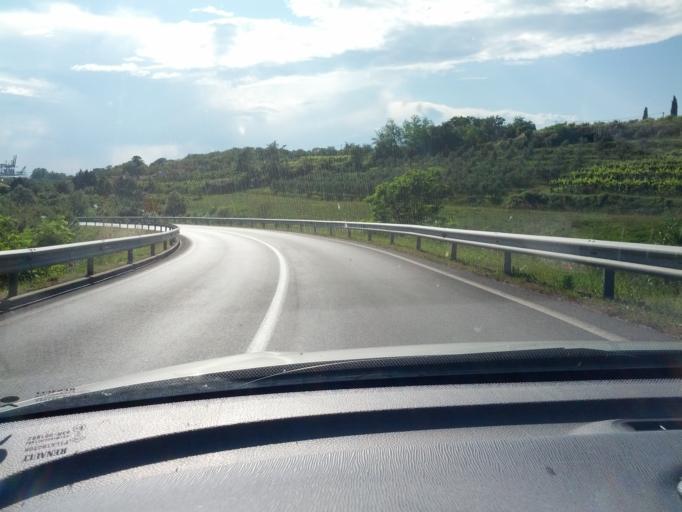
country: SI
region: Koper-Capodistria
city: Spodnje Skofije
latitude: 45.5692
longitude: 13.7788
